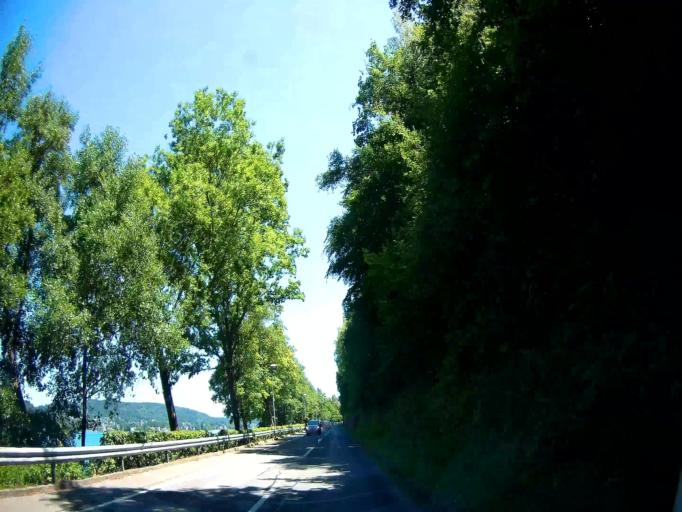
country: AT
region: Carinthia
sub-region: Politischer Bezirk Klagenfurt Land
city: Keutschach am See
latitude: 46.6076
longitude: 14.1915
